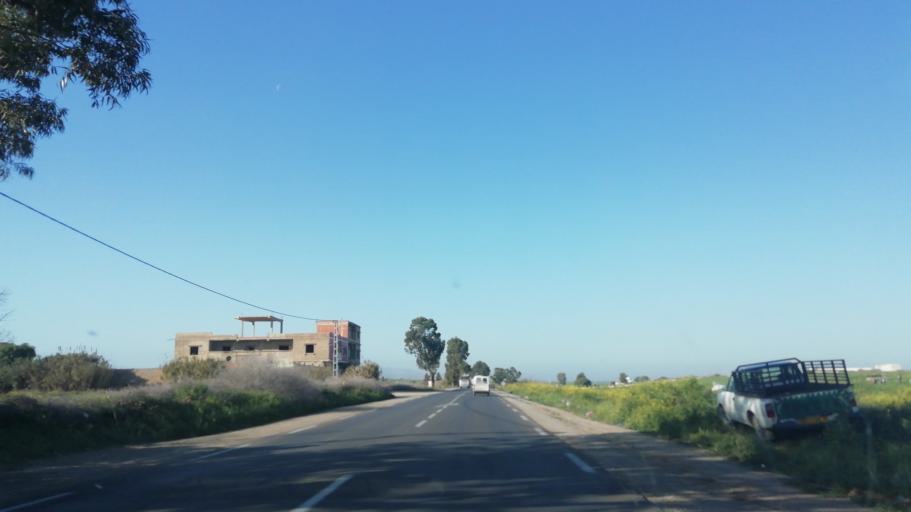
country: DZ
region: Mascara
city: Mascara
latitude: 35.6415
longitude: 0.1538
